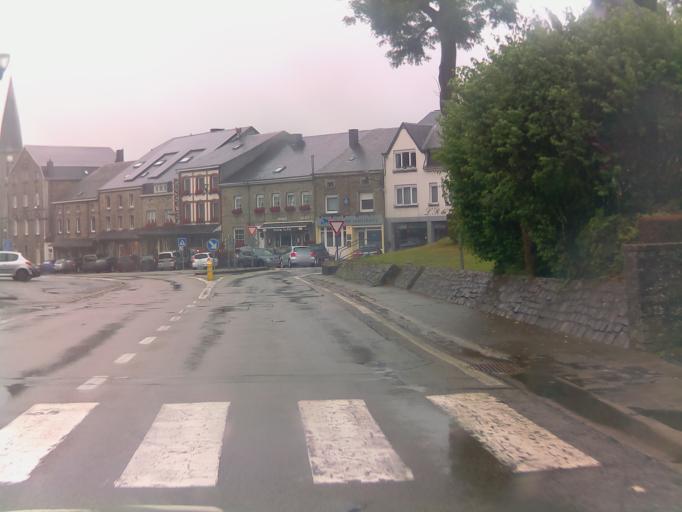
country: BE
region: Wallonia
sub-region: Province du Luxembourg
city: Paliseul
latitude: 49.9044
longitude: 5.1400
